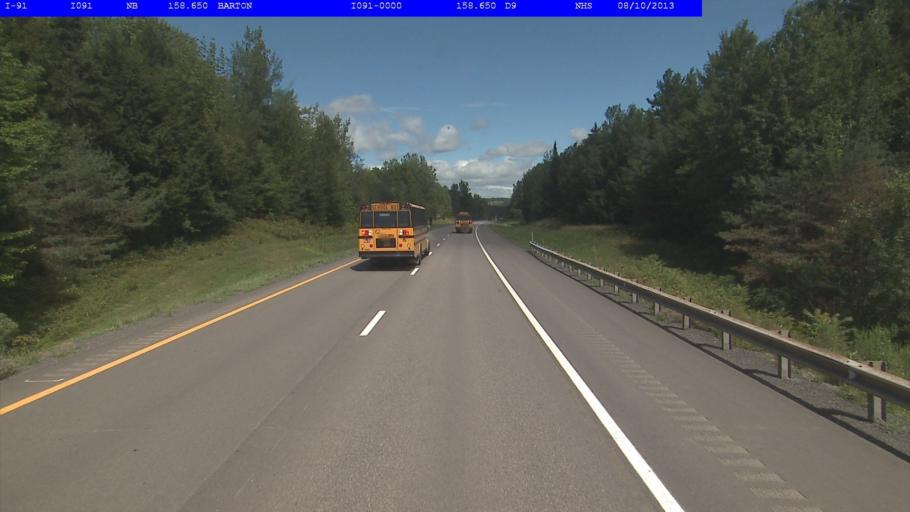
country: US
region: Vermont
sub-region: Orleans County
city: Newport
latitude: 44.7671
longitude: -72.2116
